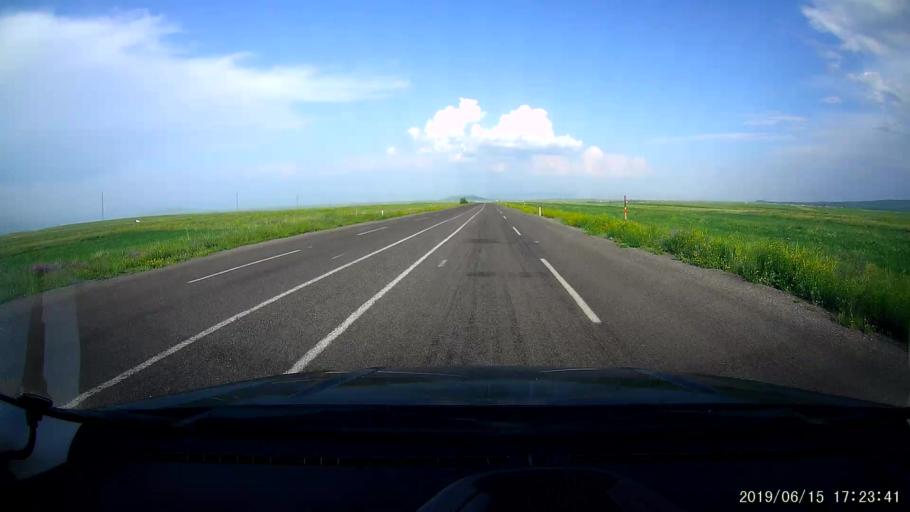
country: TR
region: Kars
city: Basgedikler
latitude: 40.6166
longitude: 43.3684
